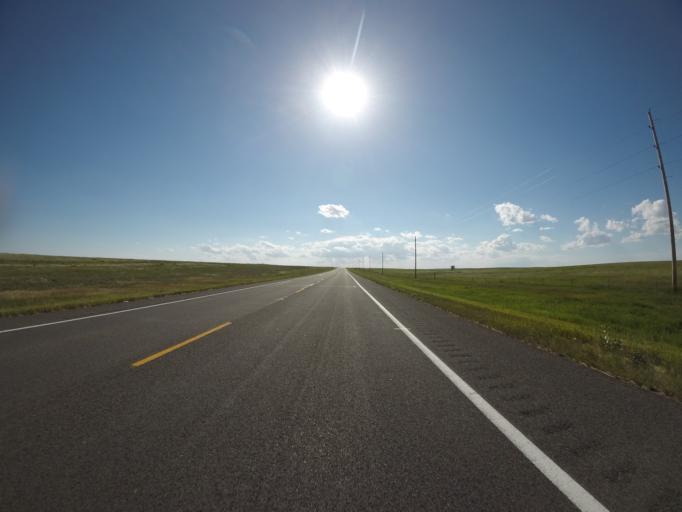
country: US
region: Colorado
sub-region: Morgan County
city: Brush
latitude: 40.6100
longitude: -103.7174
